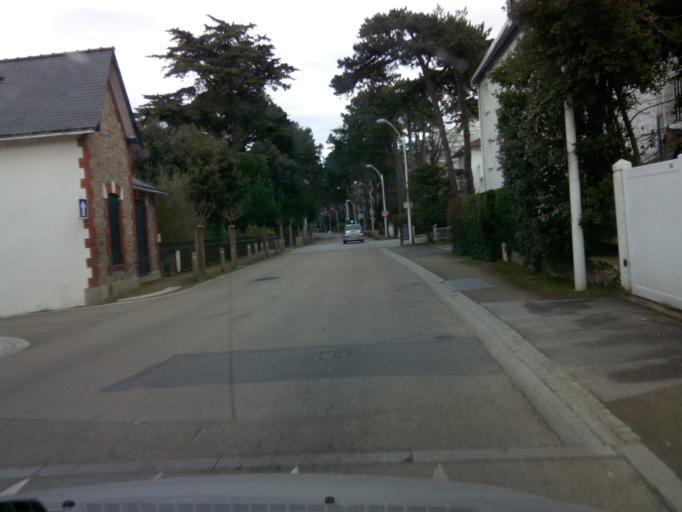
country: FR
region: Pays de la Loire
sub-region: Departement de la Loire-Atlantique
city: Le Pouliguen
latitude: 47.2778
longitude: -2.4191
